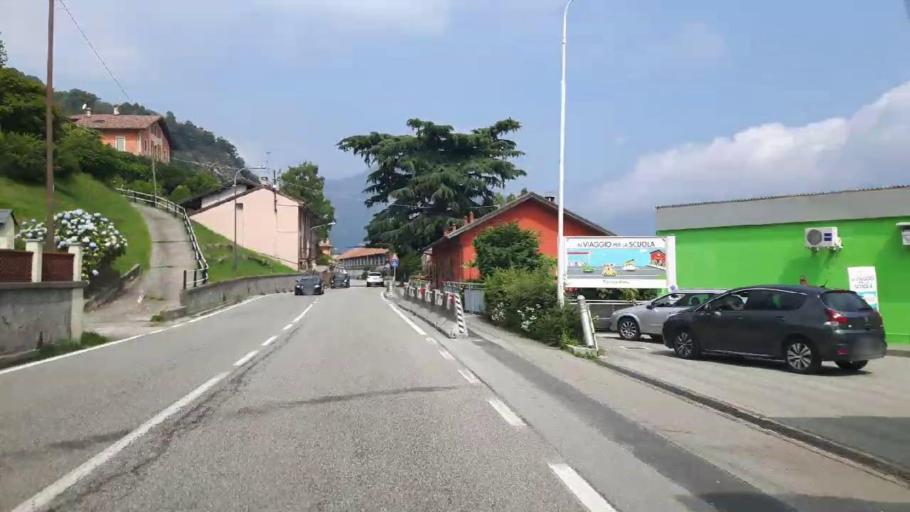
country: IT
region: Piedmont
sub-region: Provincia Verbano-Cusio-Ossola
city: Baveno
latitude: 45.9246
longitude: 8.4882
